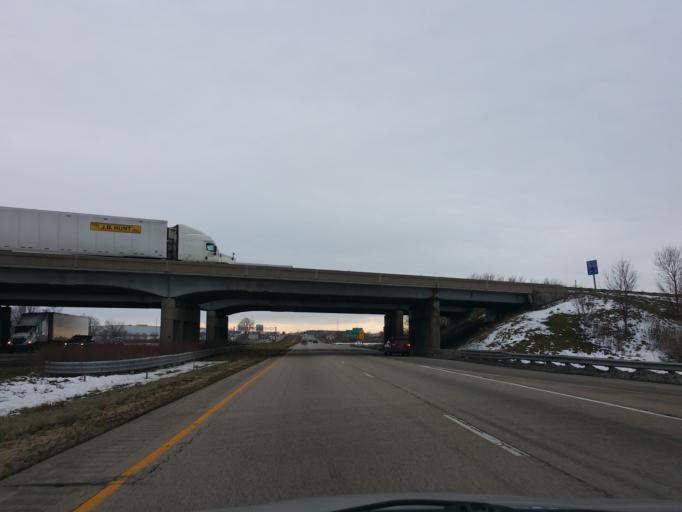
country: US
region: Wisconsin
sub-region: Rock County
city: Beloit
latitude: 42.5283
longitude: -88.9754
